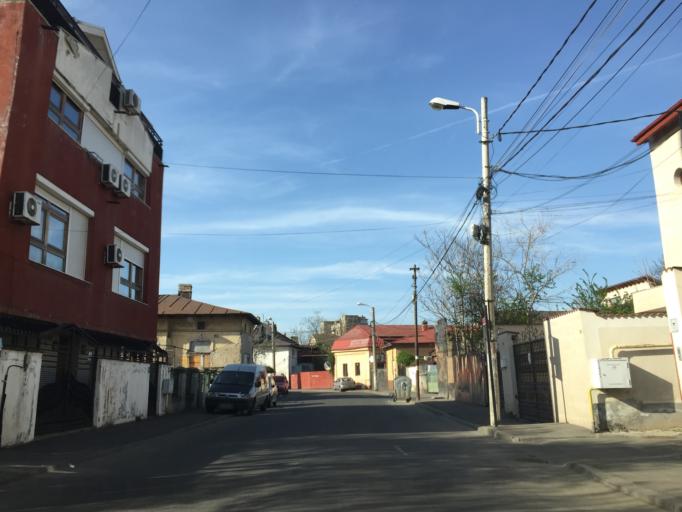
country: RO
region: Bucuresti
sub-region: Municipiul Bucuresti
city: Bucharest
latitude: 44.4283
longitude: 26.1225
